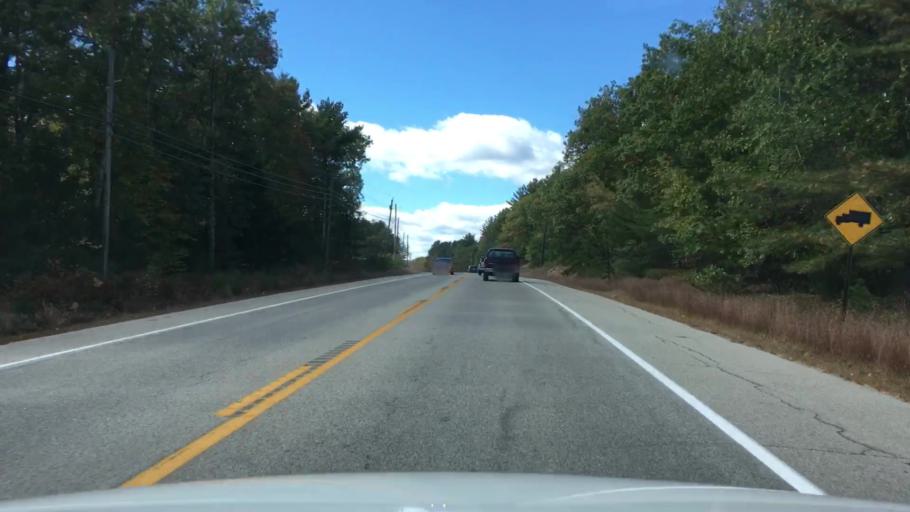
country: US
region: Maine
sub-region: York County
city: Alfred
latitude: 43.4790
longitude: -70.6348
